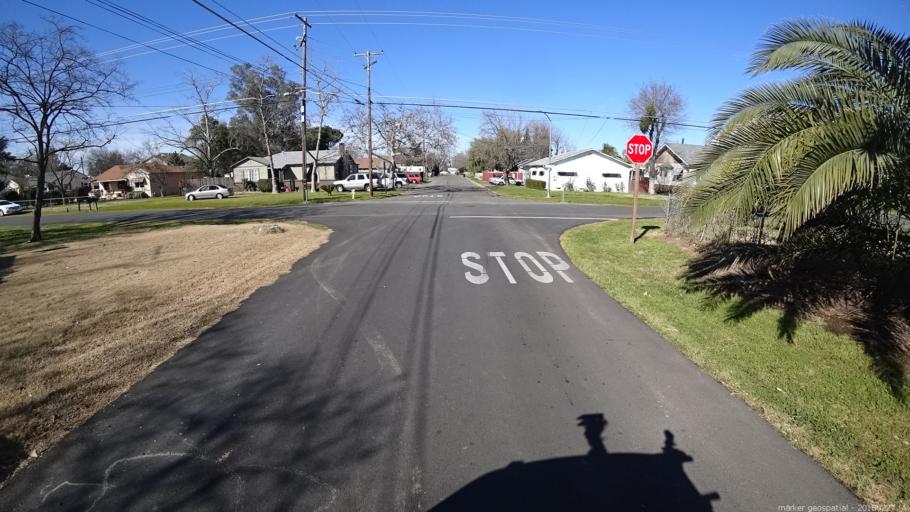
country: US
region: California
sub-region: Sacramento County
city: Rio Linda
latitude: 38.6945
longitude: -121.4442
